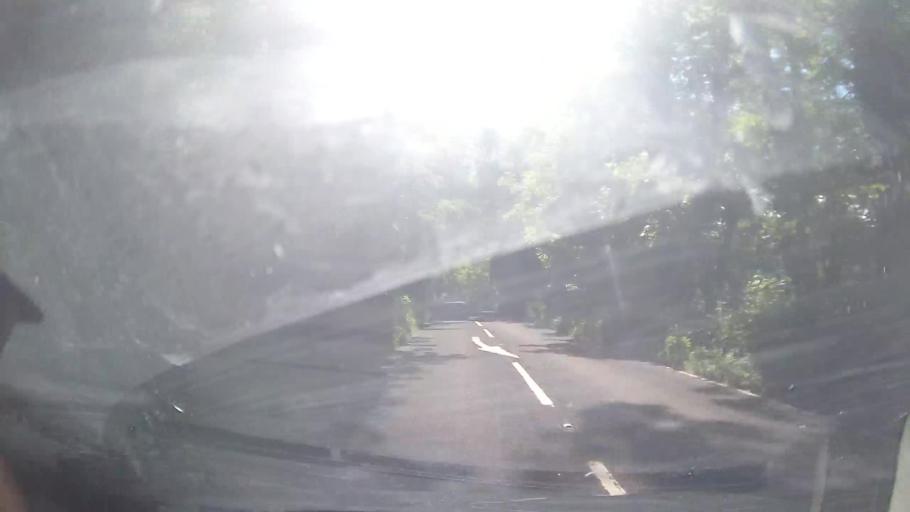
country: GB
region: England
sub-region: Devon
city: Dartmouth
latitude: 50.3674
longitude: -3.5661
